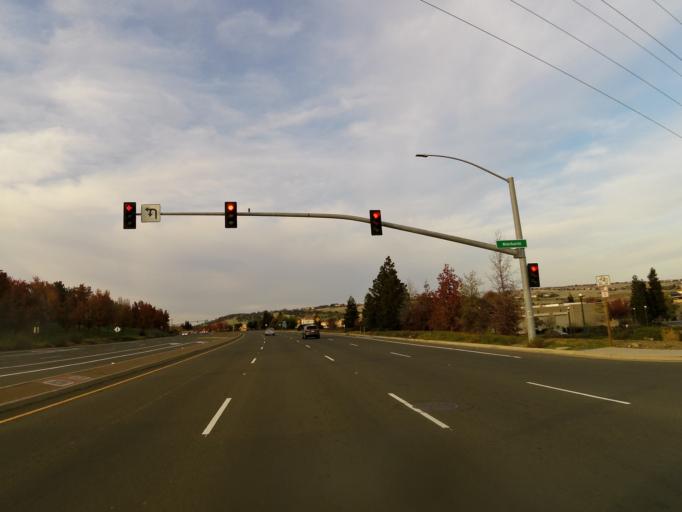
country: US
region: California
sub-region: El Dorado County
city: El Dorado Hills
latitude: 38.6470
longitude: -121.0682
